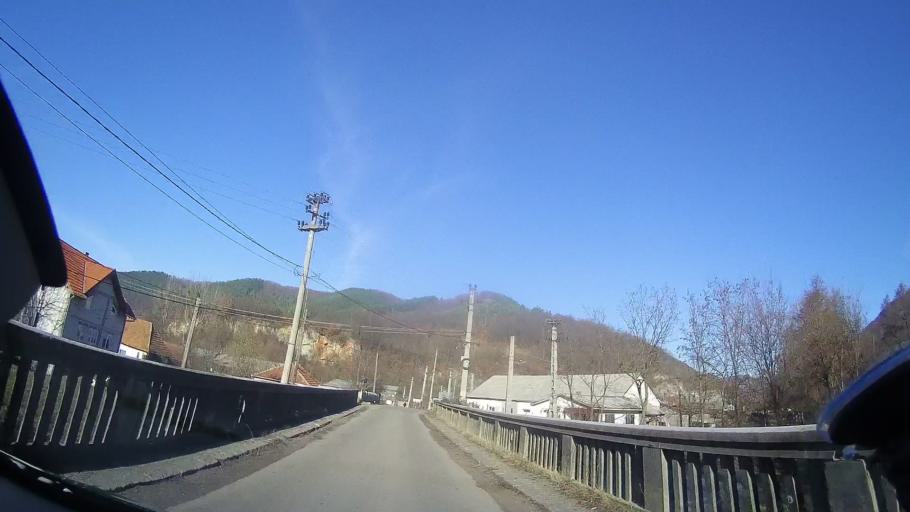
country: RO
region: Bihor
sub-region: Comuna Bulz
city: Bulz
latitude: 46.9235
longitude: 22.6537
